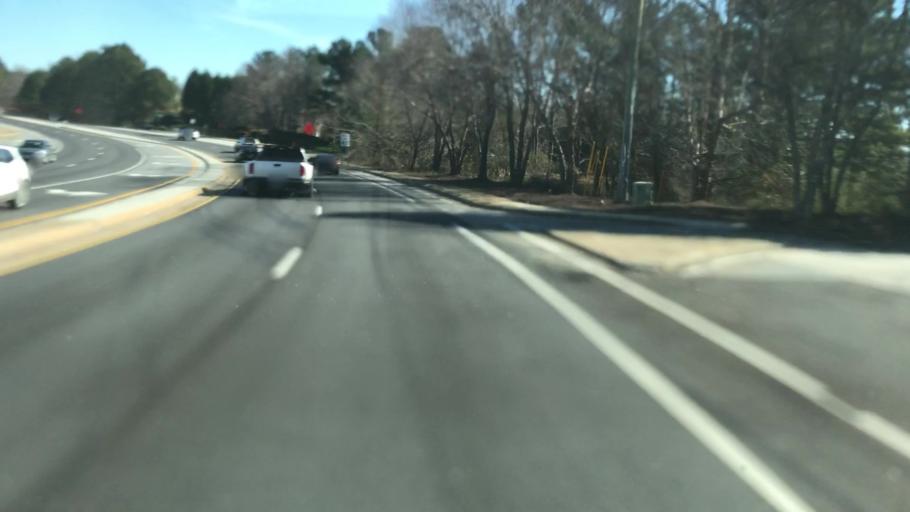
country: US
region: Georgia
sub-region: Gwinnett County
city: Lawrenceville
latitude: 33.9203
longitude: -84.0150
